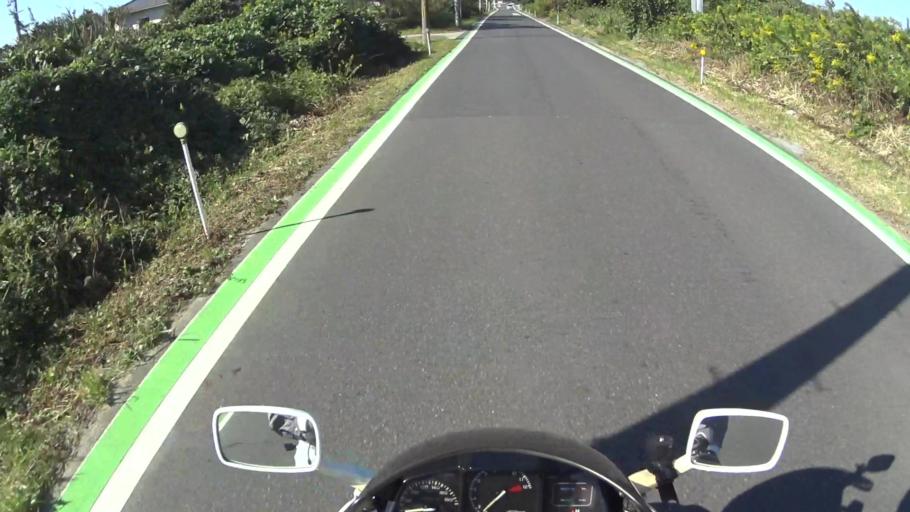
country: JP
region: Hyogo
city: Toyooka
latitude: 35.6357
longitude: 134.9287
